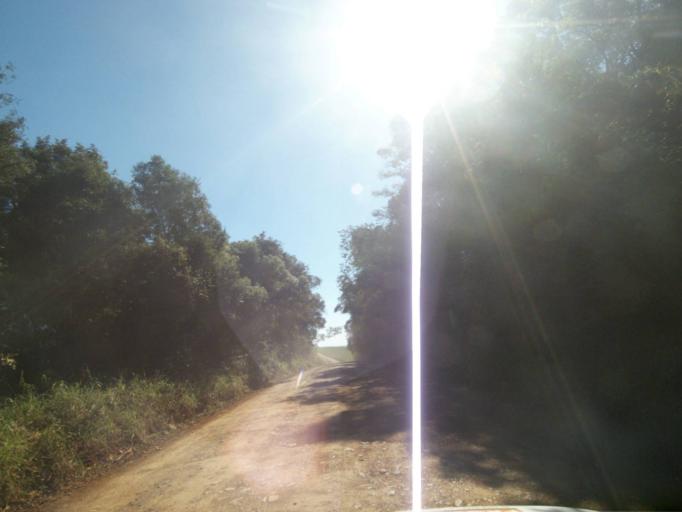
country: BR
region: Parana
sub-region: Tibagi
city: Tibagi
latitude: -24.5914
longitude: -50.6055
